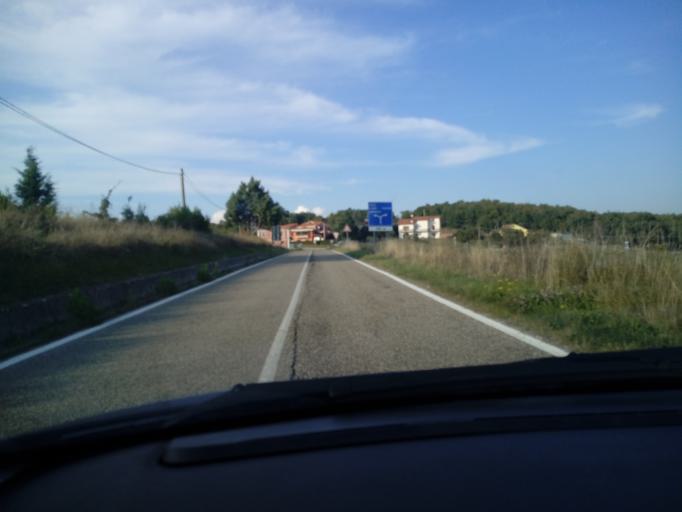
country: IT
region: Molise
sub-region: Provincia di Campobasso
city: Jelsi
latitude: 41.5091
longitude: 14.8237
